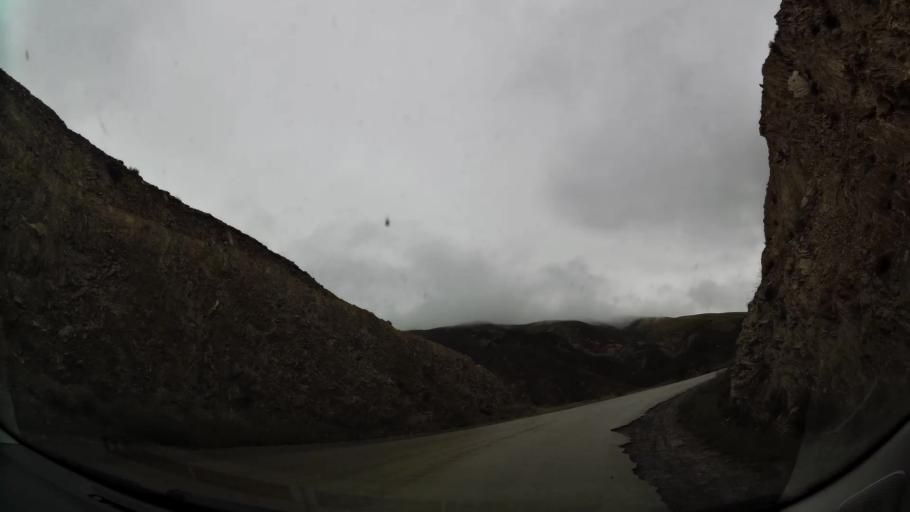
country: MA
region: Taza-Al Hoceima-Taounate
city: Imzourene
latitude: 34.9160
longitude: -3.7986
